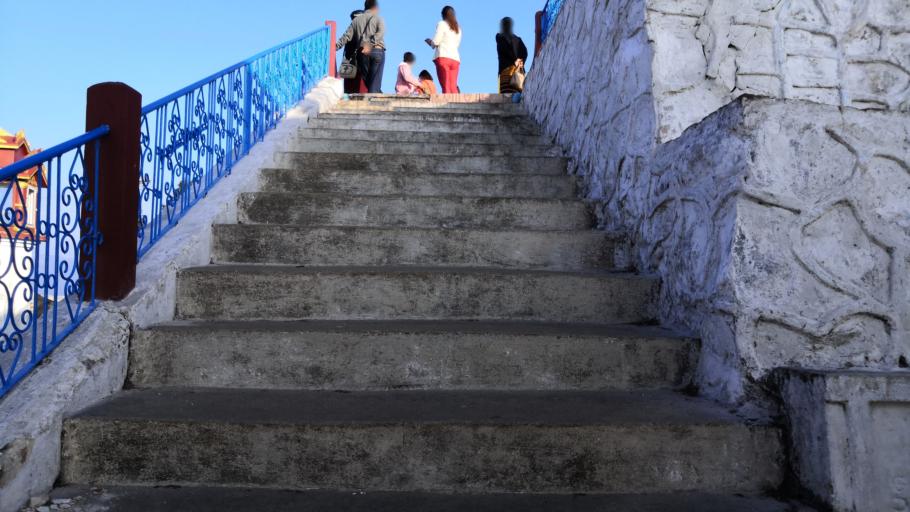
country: MM
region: Mandalay
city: Mogok
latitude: 22.8905
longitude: 96.4230
